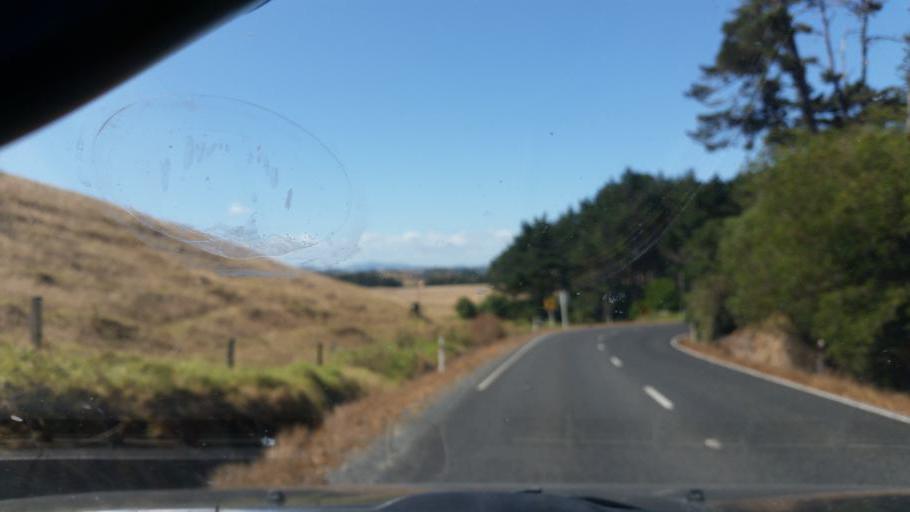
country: NZ
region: Northland
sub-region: Kaipara District
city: Dargaville
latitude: -35.9450
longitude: 173.7730
